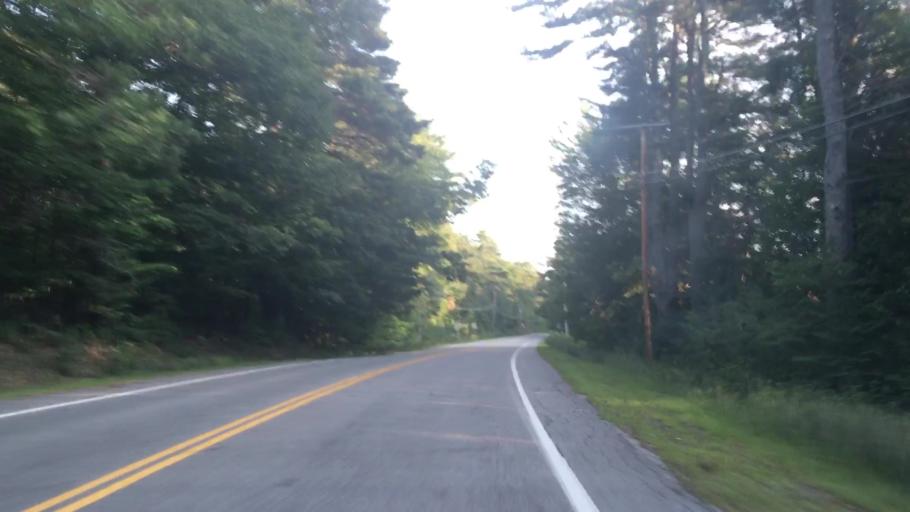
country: US
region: New Hampshire
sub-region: Belknap County
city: Gilmanton
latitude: 43.4546
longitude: -71.4214
